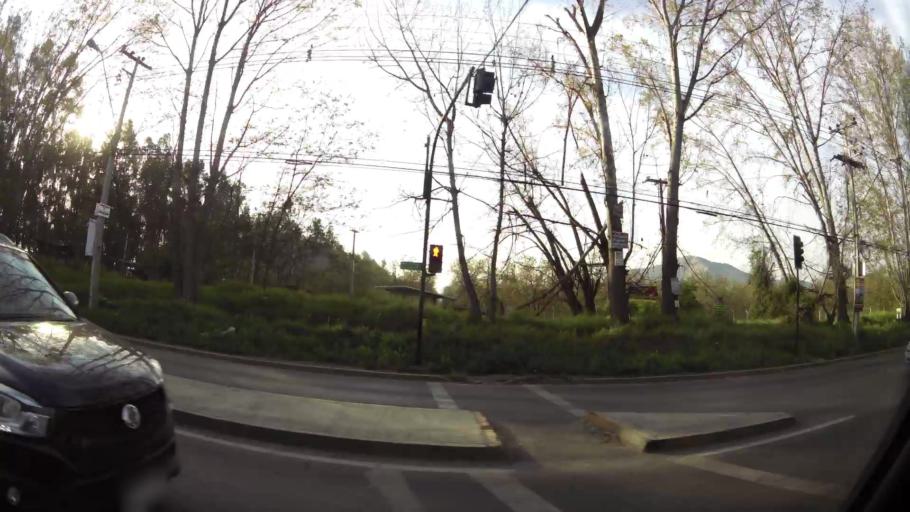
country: CL
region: Santiago Metropolitan
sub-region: Provincia de Maipo
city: San Bernardo
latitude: -33.5623
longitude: -70.7597
